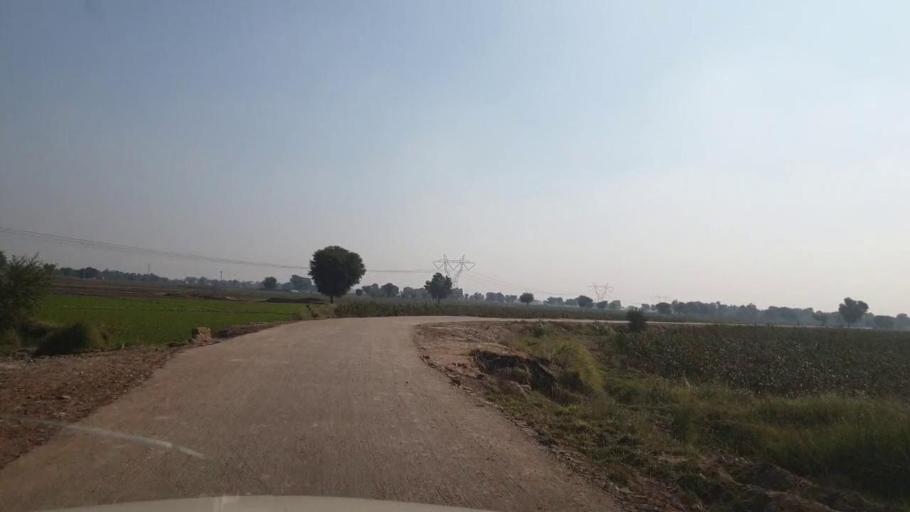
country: PK
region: Sindh
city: Bhan
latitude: 26.5366
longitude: 67.7629
